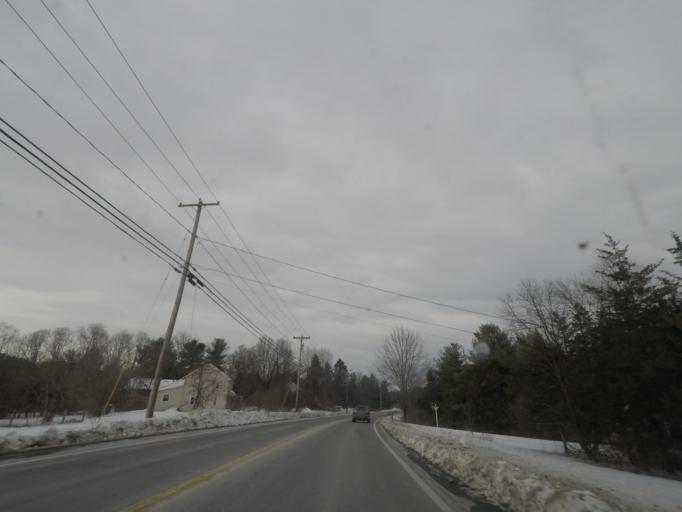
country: US
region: New York
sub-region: Columbia County
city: Kinderhook
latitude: 42.3670
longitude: -73.7337
